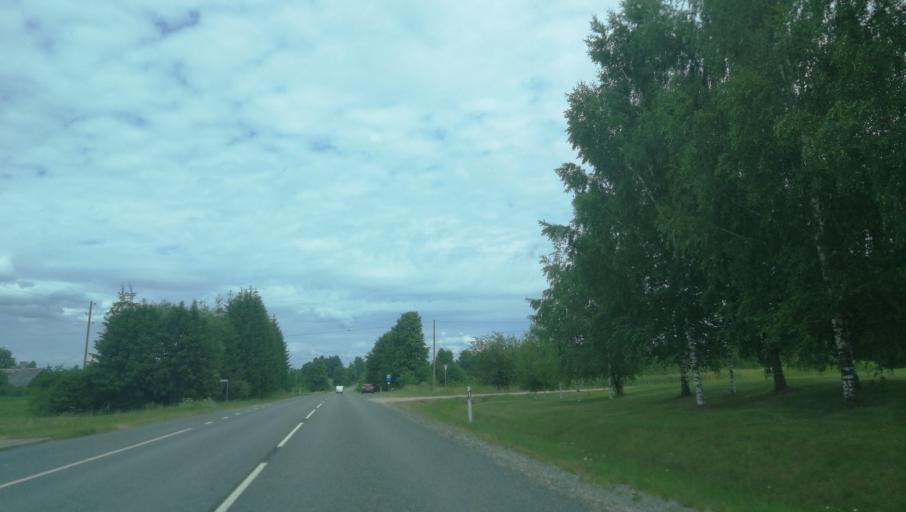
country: LV
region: Naukseni
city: Naukseni
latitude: 57.7290
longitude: 25.4226
